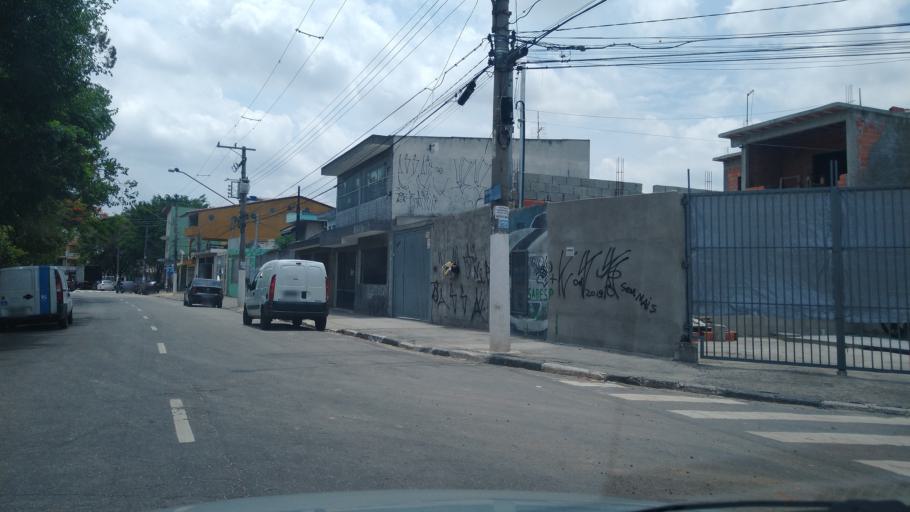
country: BR
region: Sao Paulo
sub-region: Osasco
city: Osasco
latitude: -23.5114
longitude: -46.7805
